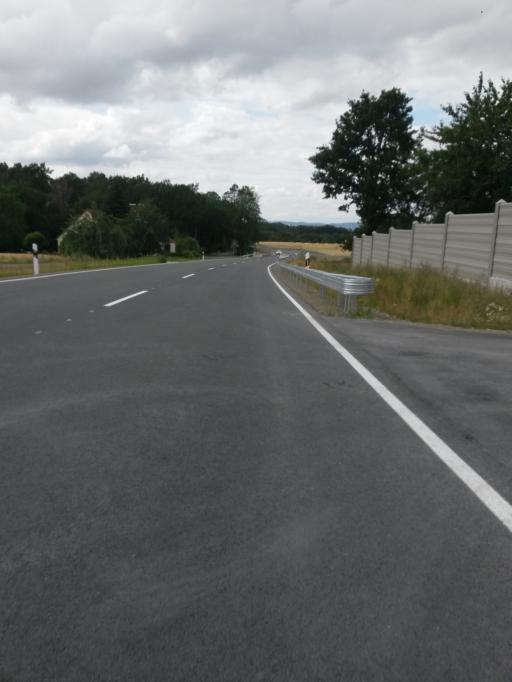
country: DE
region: North Rhine-Westphalia
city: Bad Oeynhausen
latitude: 52.1596
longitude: 8.7658
